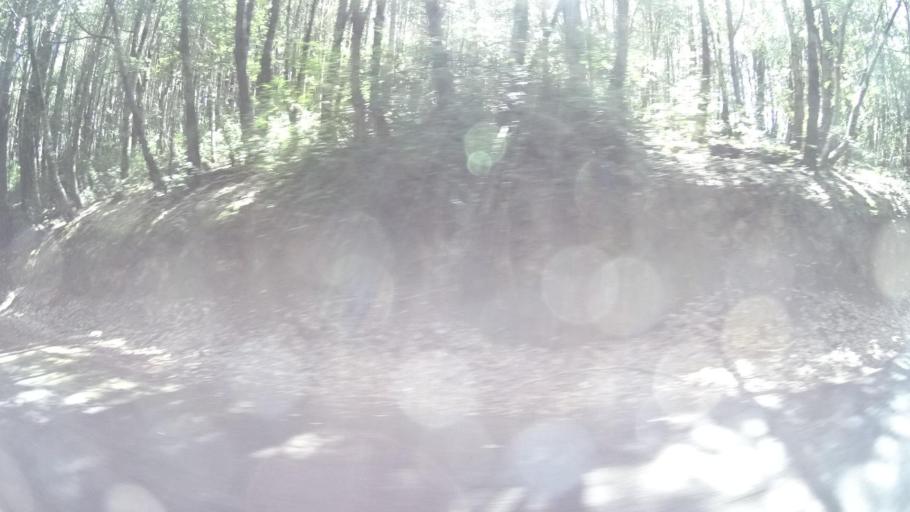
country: US
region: California
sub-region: Humboldt County
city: Rio Dell
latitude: 40.2065
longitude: -124.1032
